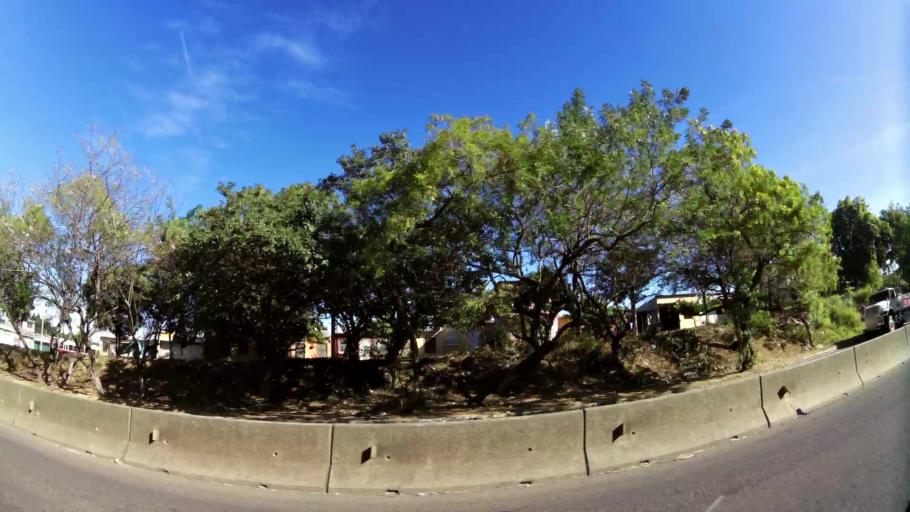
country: SV
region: Santa Ana
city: Santa Ana
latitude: 13.9554
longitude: -89.5725
